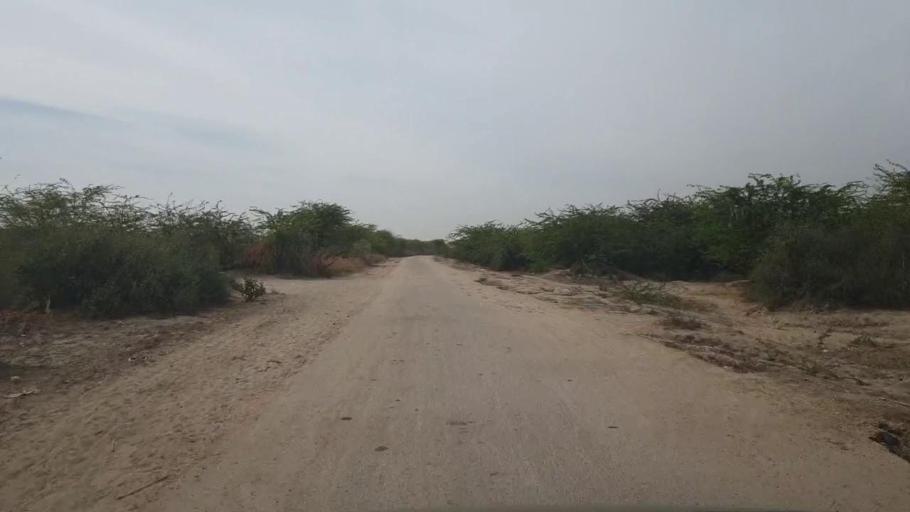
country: PK
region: Sindh
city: Umarkot
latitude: 25.2512
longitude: 69.7202
